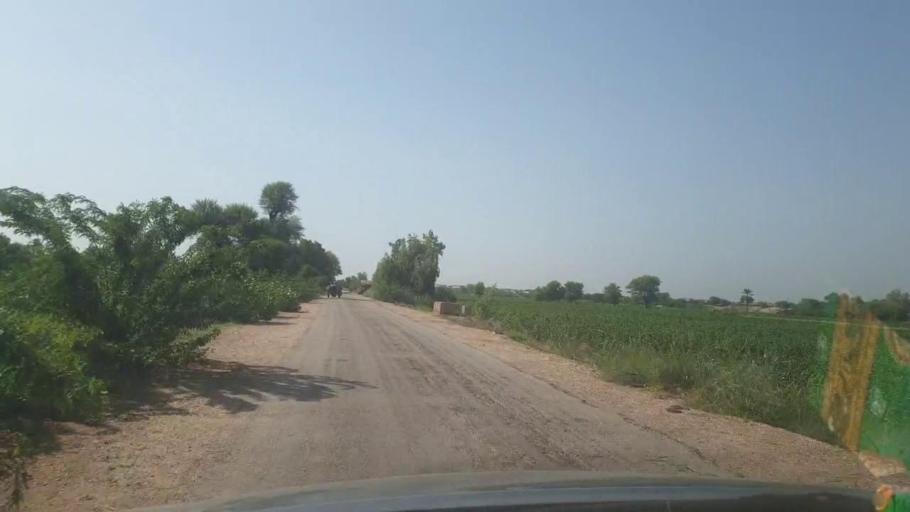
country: PK
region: Sindh
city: Rohri
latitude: 27.4689
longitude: 69.0366
